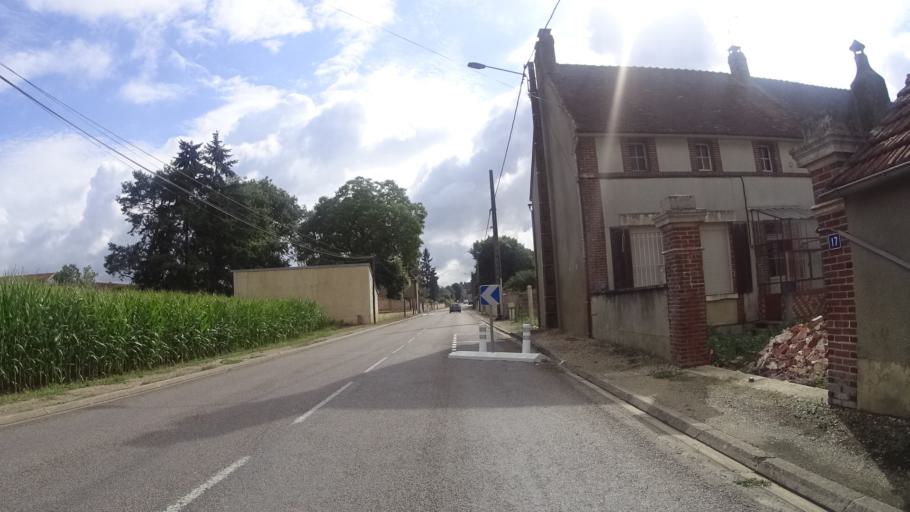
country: FR
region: Bourgogne
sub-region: Departement de l'Yonne
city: Vergigny
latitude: 47.9714
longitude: 3.7153
